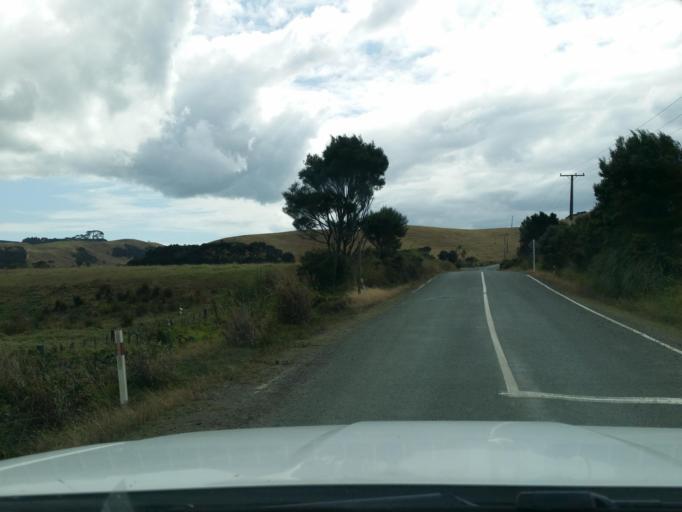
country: NZ
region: Auckland
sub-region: Auckland
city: Wellsford
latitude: -36.2986
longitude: 174.1071
